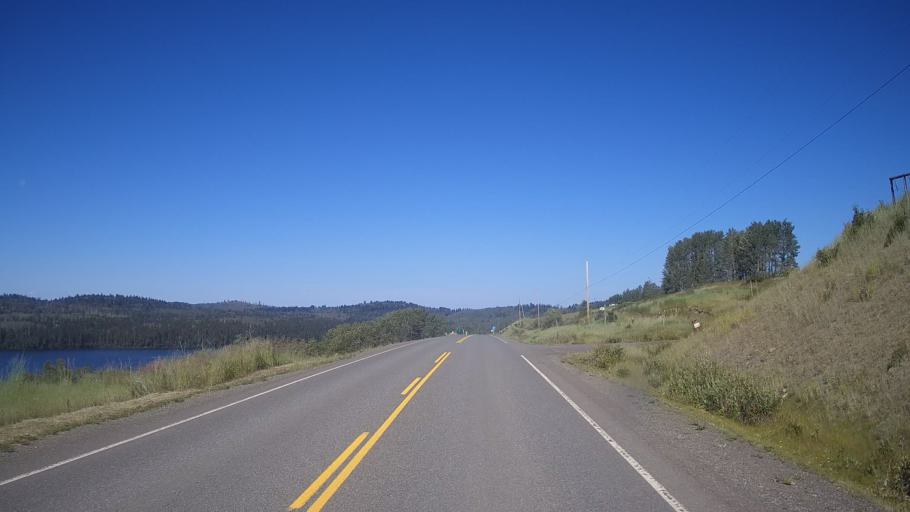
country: CA
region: British Columbia
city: Kamloops
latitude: 51.4981
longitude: -120.5889
